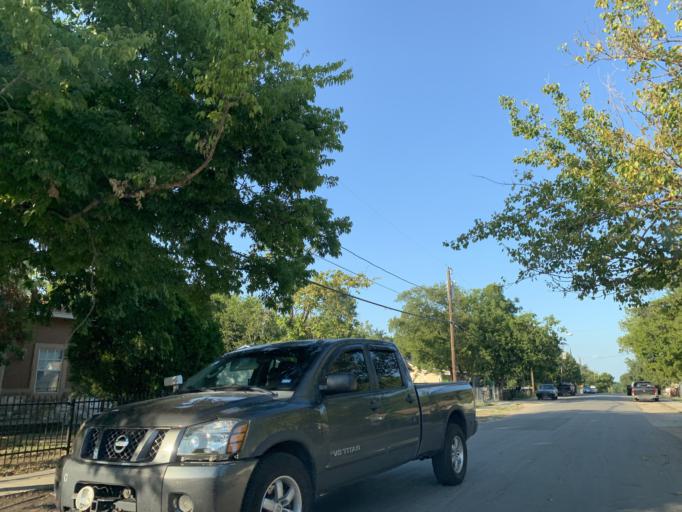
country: US
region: Texas
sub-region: Dallas County
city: Dallas
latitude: 32.7017
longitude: -96.7861
